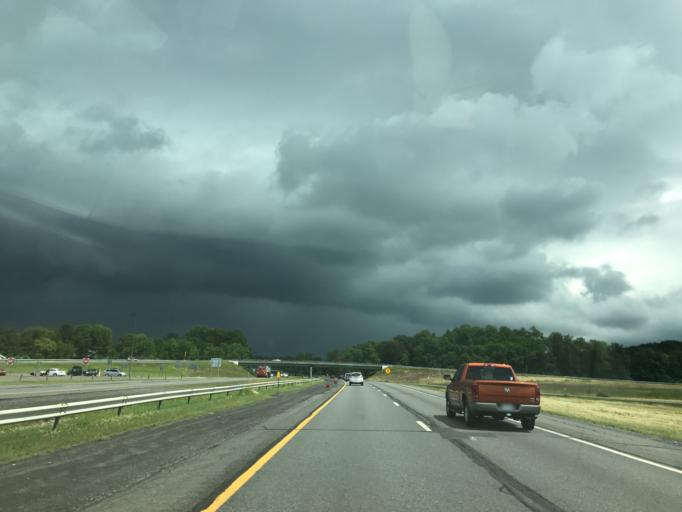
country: US
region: New York
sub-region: Albany County
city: Ravena
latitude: 42.4274
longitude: -73.8047
